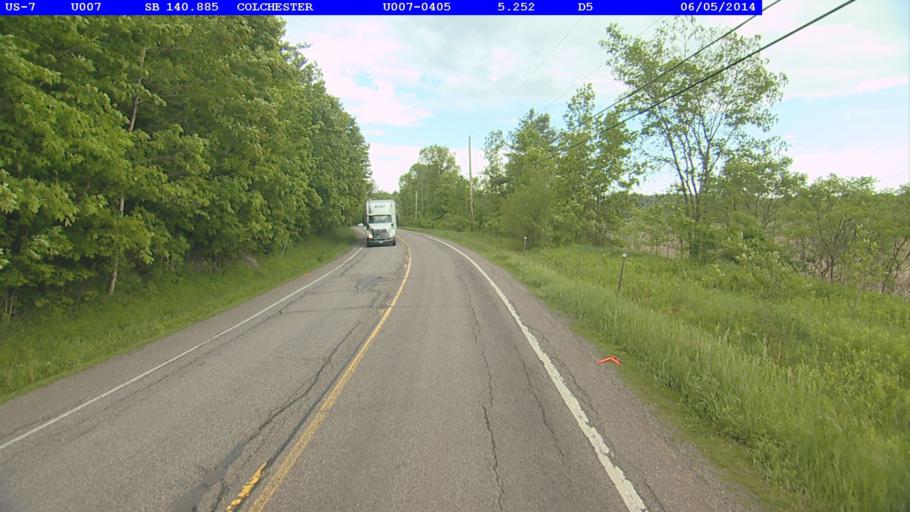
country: US
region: Vermont
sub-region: Chittenden County
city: Colchester
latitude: 44.5729
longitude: -73.1574
